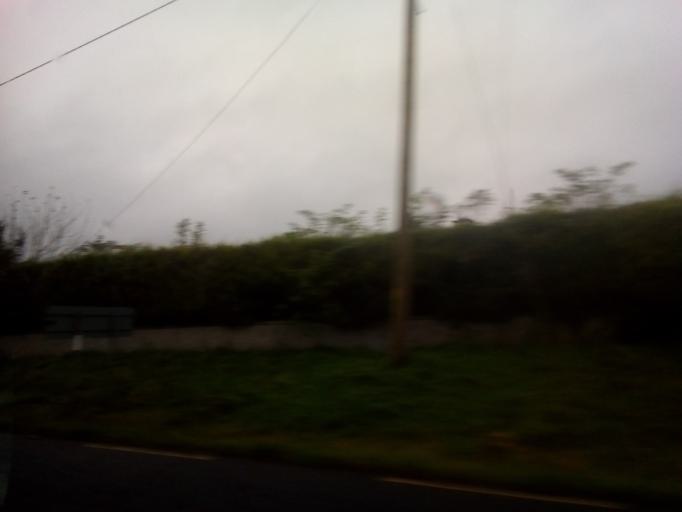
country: IE
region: Connaught
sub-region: Roscommon
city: Roscommon
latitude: 53.7663
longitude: -8.1714
